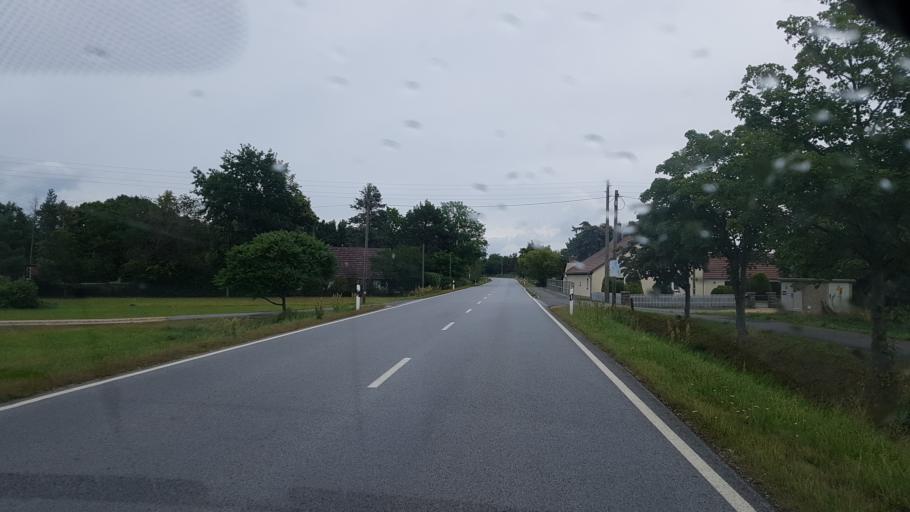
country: DE
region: Saxony
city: Quitzdorf
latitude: 51.2257
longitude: 14.7865
